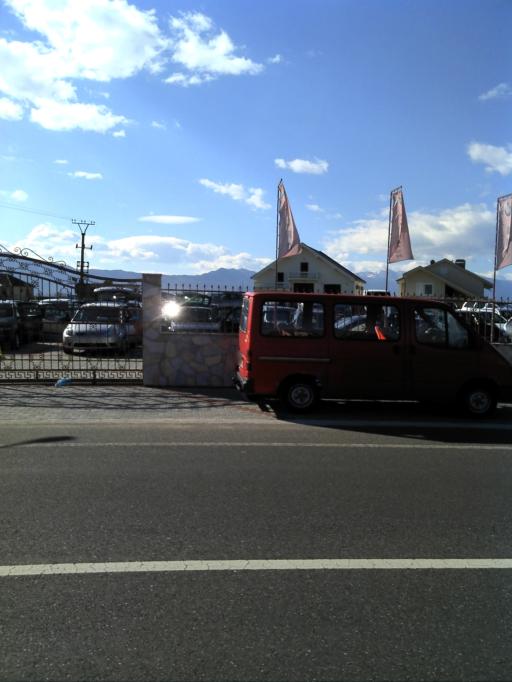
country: AL
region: Shkoder
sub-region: Rrethi i Shkodres
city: Shkoder
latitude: 42.1096
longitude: 19.5017
